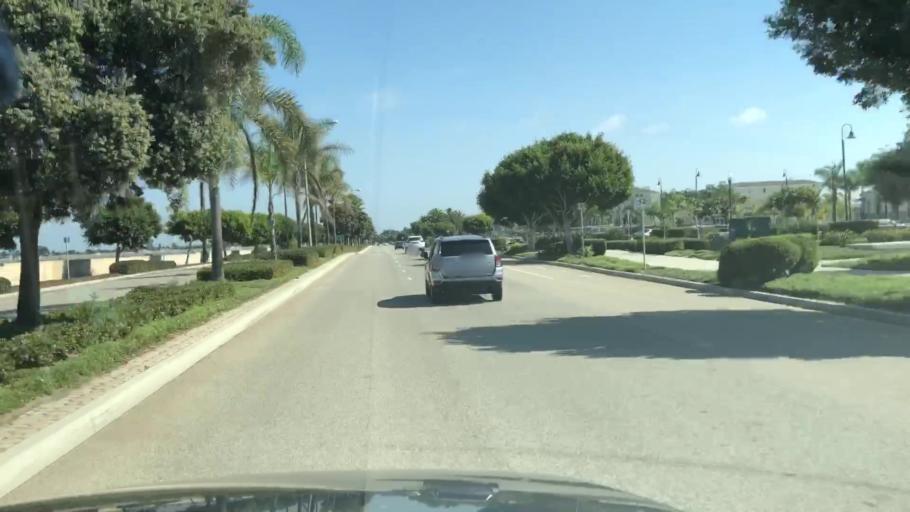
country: US
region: California
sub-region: Ventura County
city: Oxnard Shores
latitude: 34.1903
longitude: -119.2313
